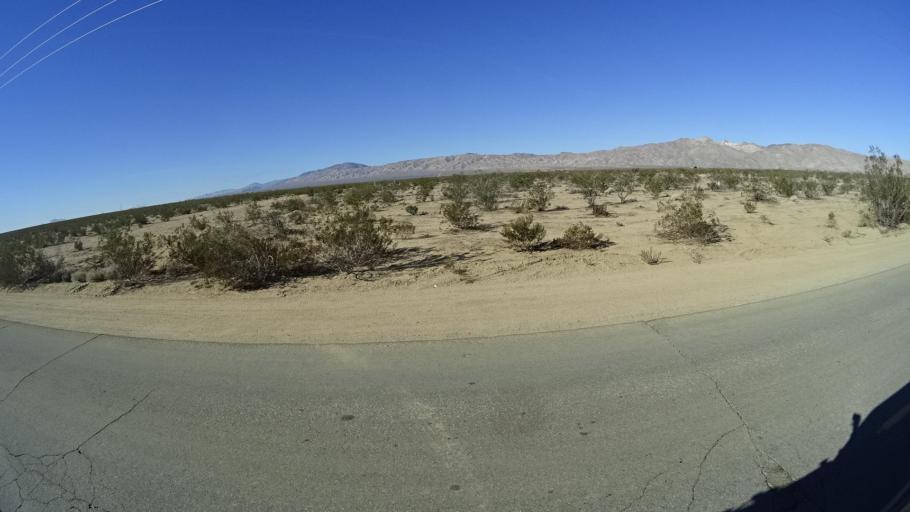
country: US
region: California
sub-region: Kern County
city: California City
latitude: 35.2144
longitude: -117.9858
